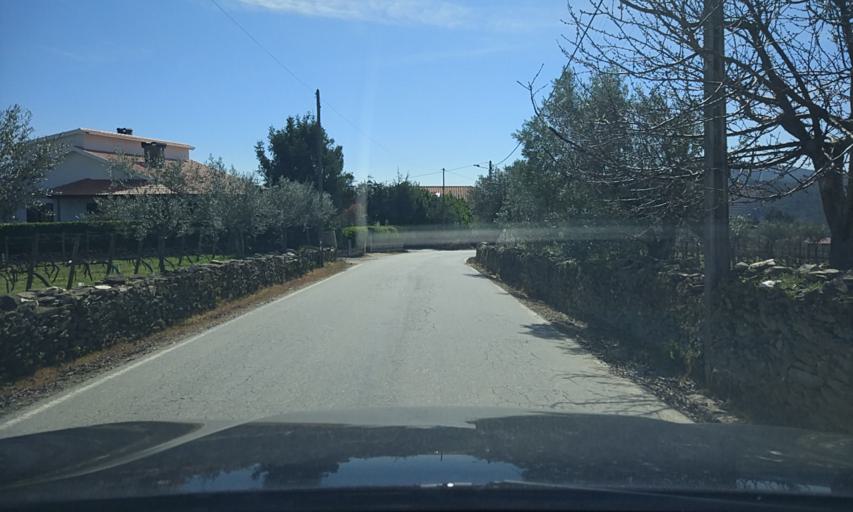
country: PT
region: Vila Real
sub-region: Sabrosa
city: Sabrosa
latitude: 41.3108
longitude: -7.5603
